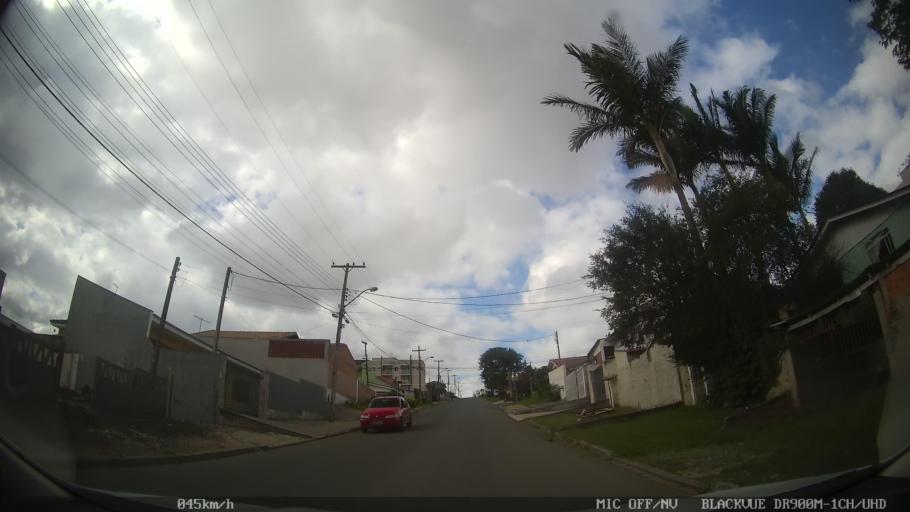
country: BR
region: Parana
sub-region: Colombo
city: Colombo
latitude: -25.3572
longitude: -49.2048
